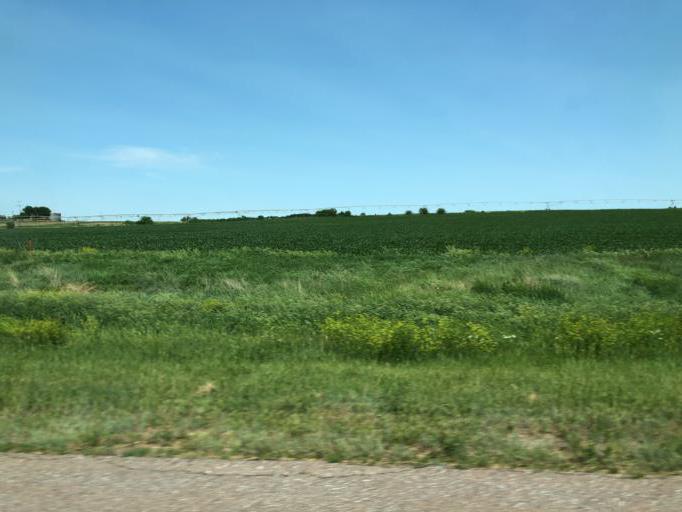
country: US
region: Nebraska
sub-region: York County
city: York
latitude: 40.7107
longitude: -97.5952
